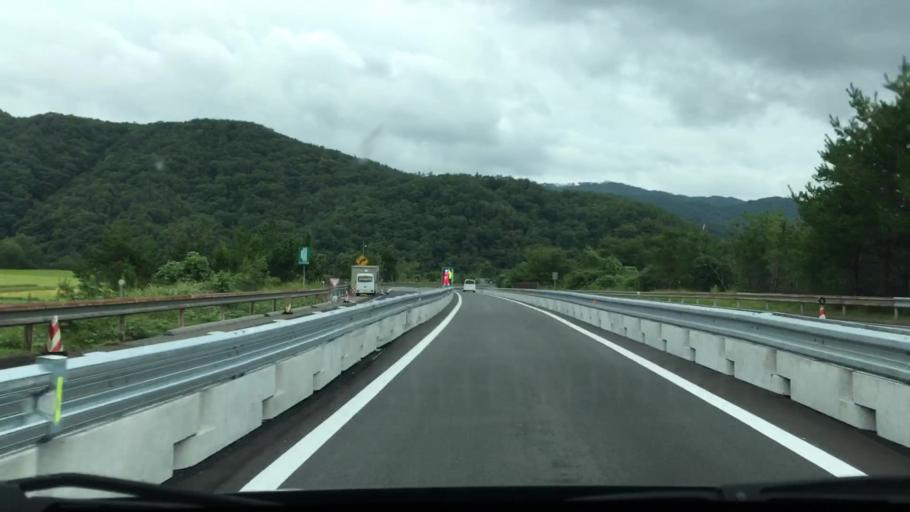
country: JP
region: Hiroshima
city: Miyoshi
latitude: 34.7315
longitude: 132.7052
